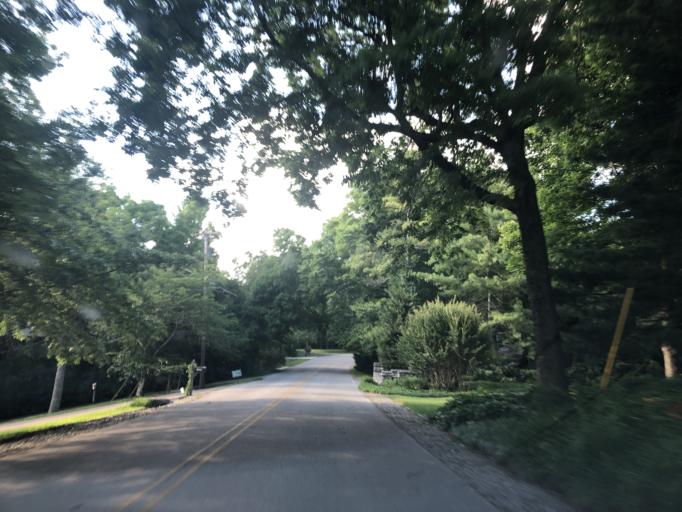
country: US
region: Tennessee
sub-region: Davidson County
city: Forest Hills
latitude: 36.0710
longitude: -86.8178
